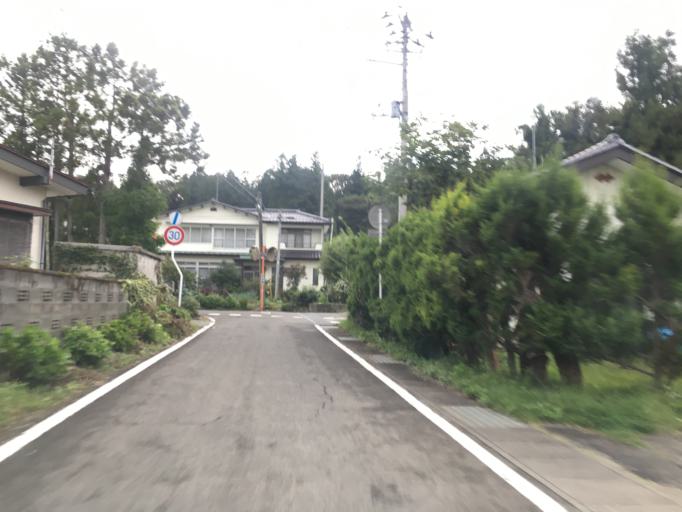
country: JP
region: Fukushima
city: Nihommatsu
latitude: 37.6550
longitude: 140.4446
